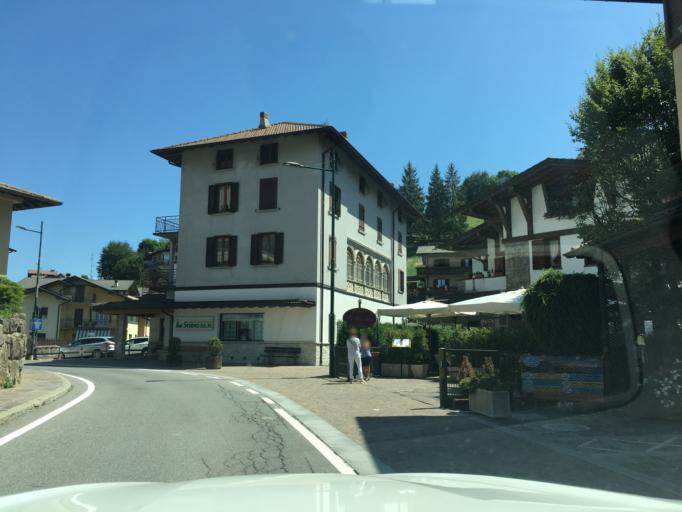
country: IT
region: Lombardy
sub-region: Provincia di Bergamo
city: Selvino
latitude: 45.7824
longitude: 9.7564
